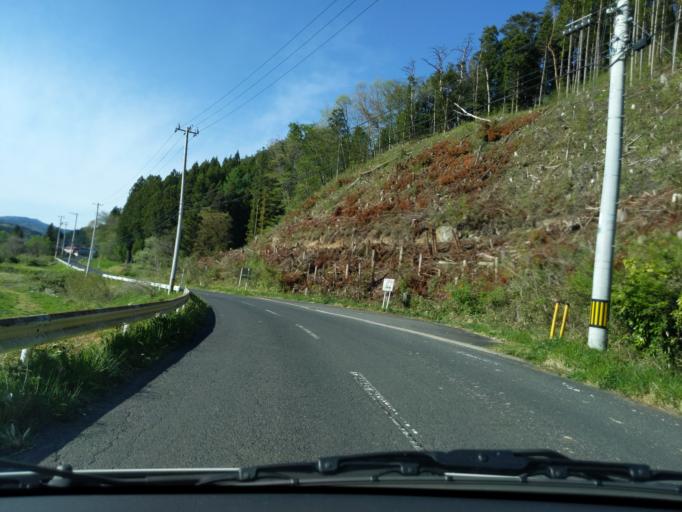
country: JP
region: Iwate
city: Ichinoseki
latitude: 38.8324
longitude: 140.9121
